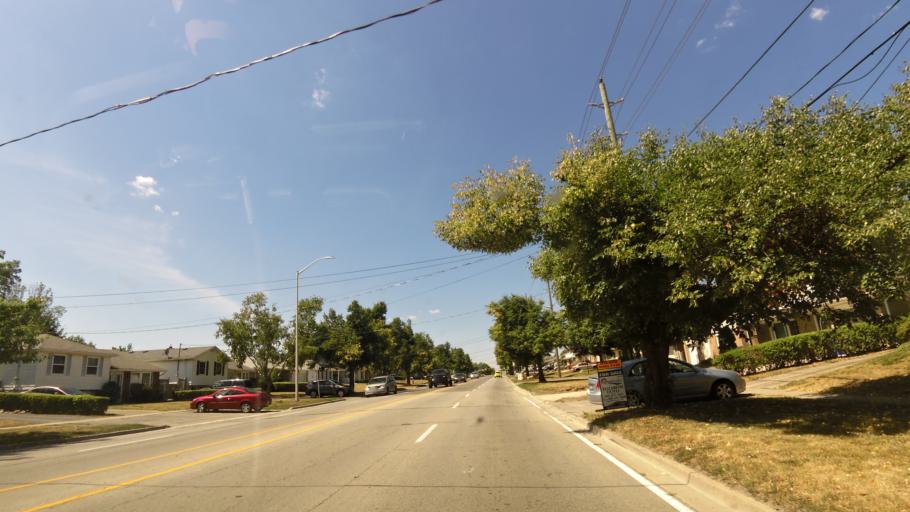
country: CA
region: Ontario
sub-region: Halton
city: Milton
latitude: 43.6406
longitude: -79.8903
